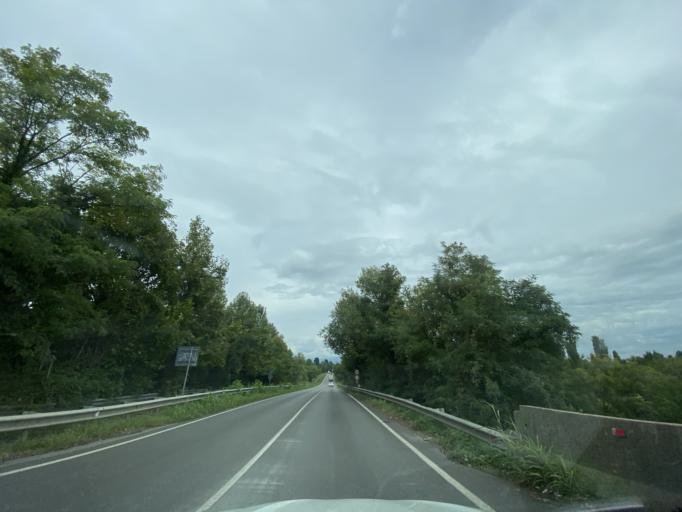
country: IT
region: Lombardy
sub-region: Citta metropolitana di Milano
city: Ronco
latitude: 45.5212
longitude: 9.3489
